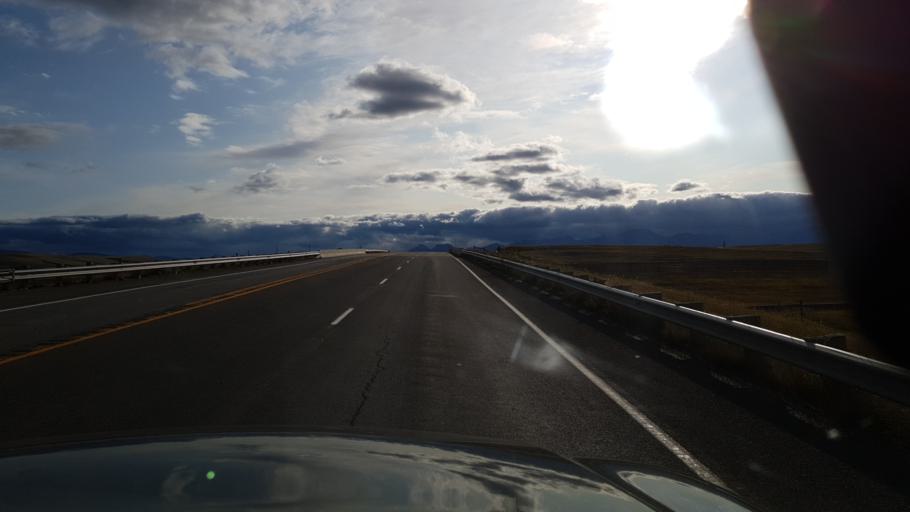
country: US
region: Montana
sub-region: Glacier County
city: South Browning
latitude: 48.5421
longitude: -113.0331
